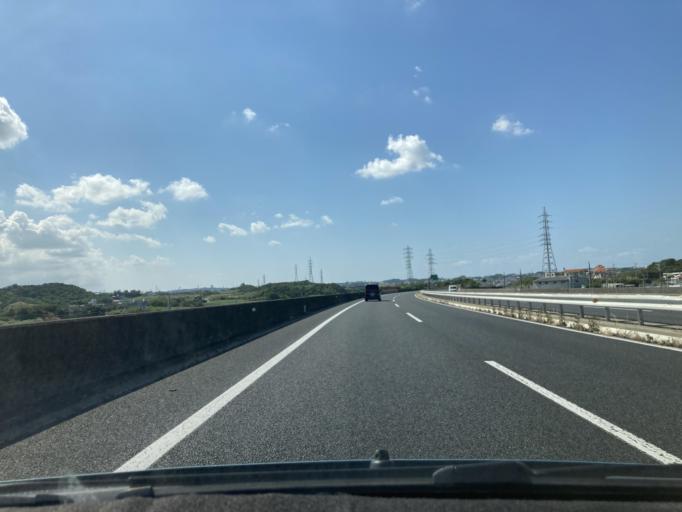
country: JP
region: Okinawa
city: Tomigusuku
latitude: 26.1847
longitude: 127.7358
